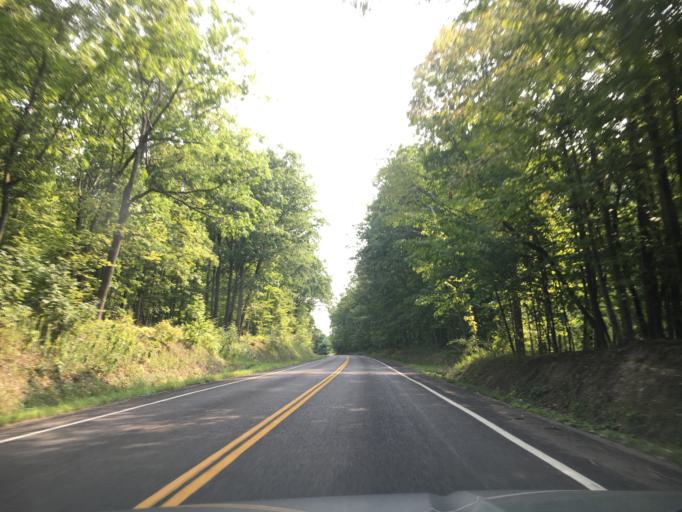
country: US
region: New York
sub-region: Steuben County
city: Sylvan Beach
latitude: 42.4812
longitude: -77.1258
